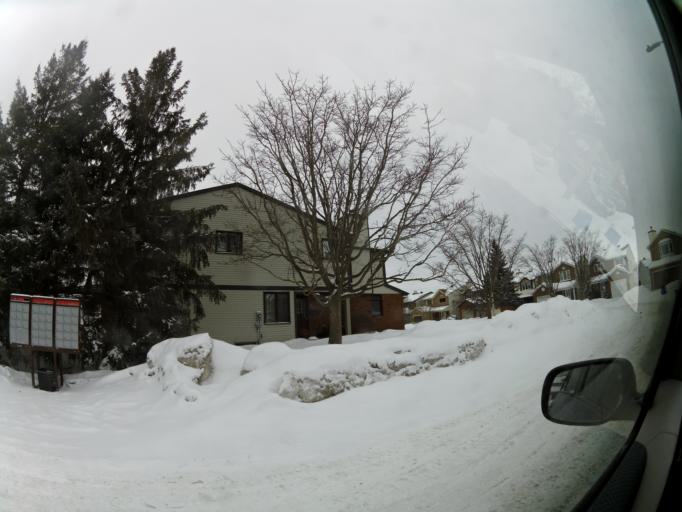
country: CA
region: Ontario
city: Ottawa
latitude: 45.3706
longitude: -75.6076
